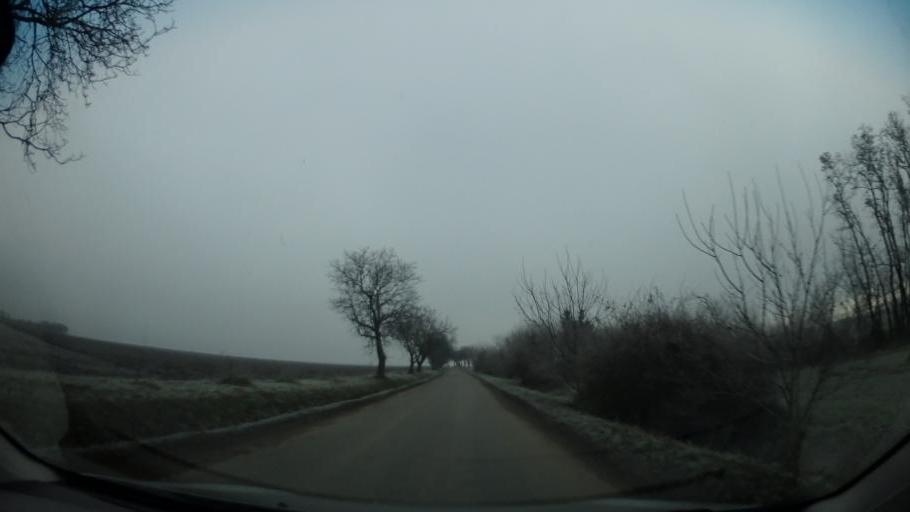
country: CZ
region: Vysocina
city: Mohelno
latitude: 49.1201
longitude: 16.2108
